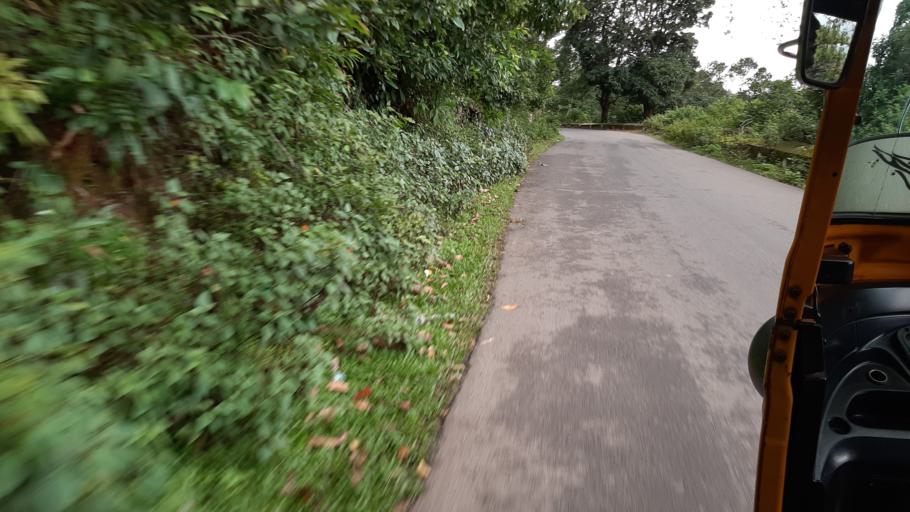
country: IN
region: Andhra Pradesh
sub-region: Vizianagaram District
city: Salur
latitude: 18.2398
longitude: 83.0158
